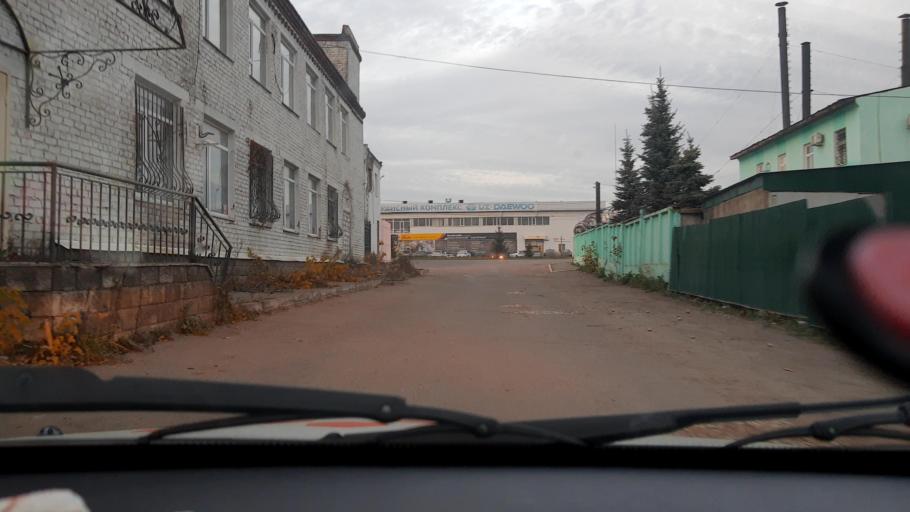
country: RU
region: Bashkortostan
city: Ufa
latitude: 54.8053
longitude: 56.0867
